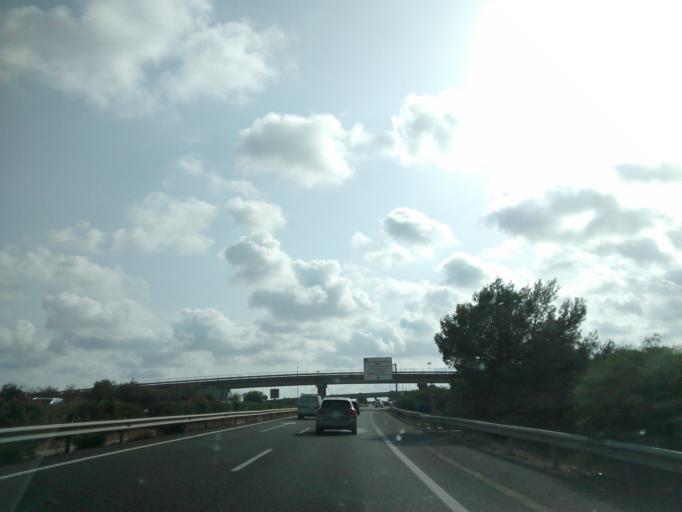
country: ES
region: Valencia
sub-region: Provincia de Alicante
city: el Campello
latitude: 38.4244
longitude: -0.4189
